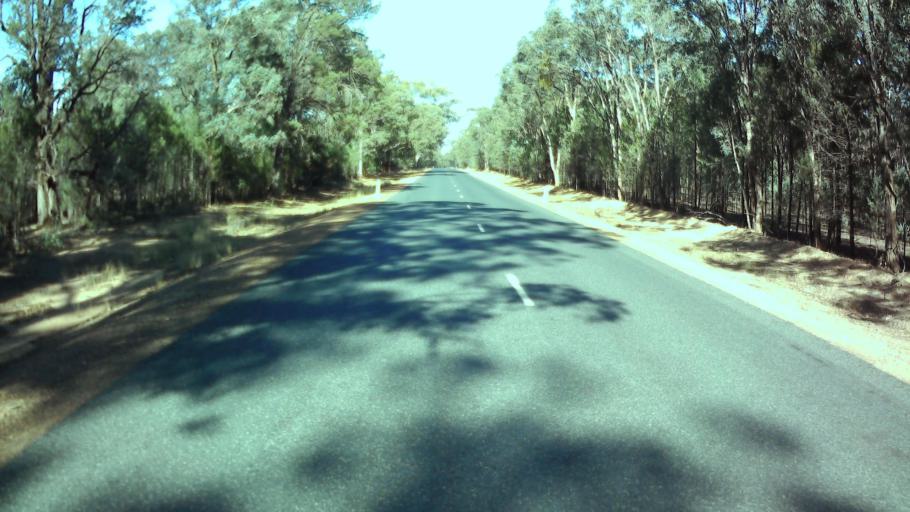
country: AU
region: New South Wales
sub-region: Weddin
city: Grenfell
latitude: -34.0248
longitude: 148.0117
